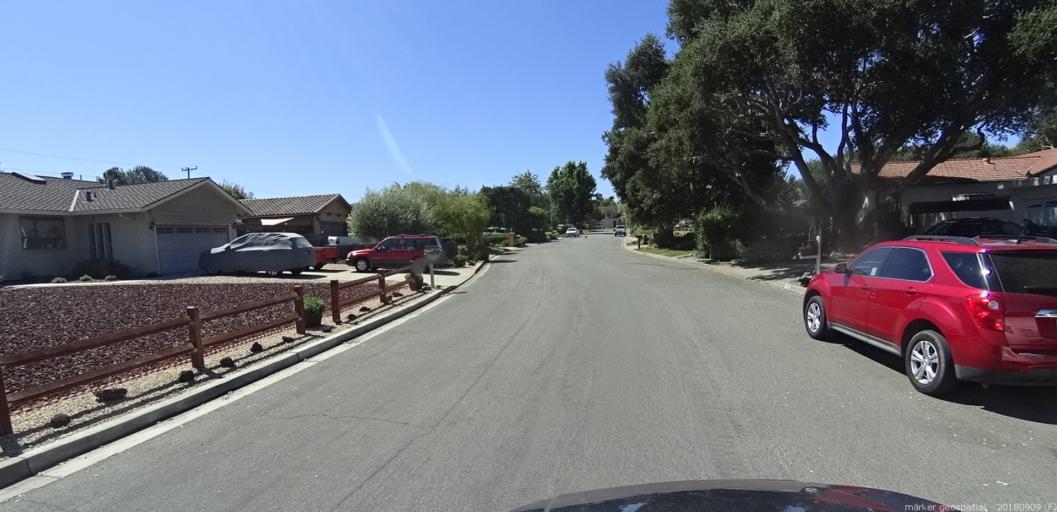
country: US
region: California
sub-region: Monterey County
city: Salinas
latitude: 36.6100
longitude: -121.6944
